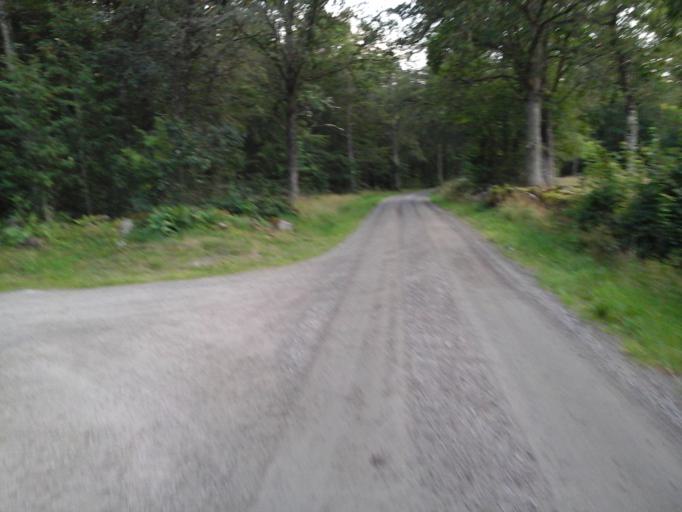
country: SE
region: Kronoberg
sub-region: Ljungby Kommun
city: Lagan
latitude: 56.9637
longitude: 13.8560
